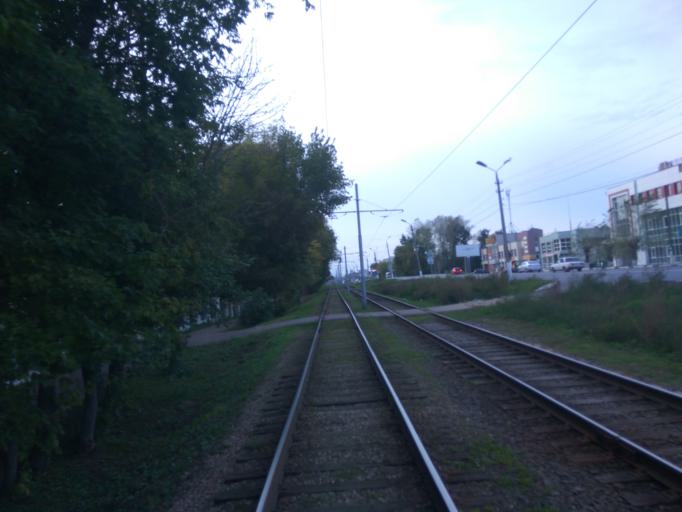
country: RU
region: Moskovskaya
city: Kolomna
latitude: 55.0809
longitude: 38.8140
